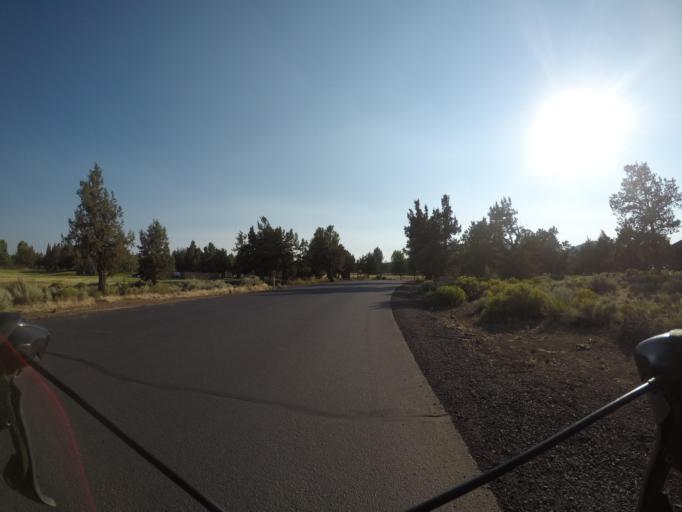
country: US
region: Oregon
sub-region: Deschutes County
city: Redmond
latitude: 44.2619
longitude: -121.2622
